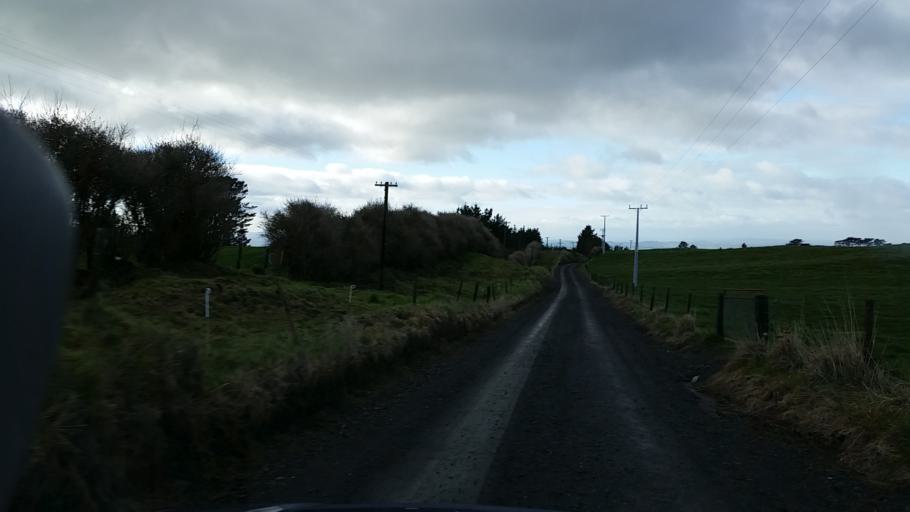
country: NZ
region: Taranaki
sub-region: South Taranaki District
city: Eltham
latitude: -39.3344
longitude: 174.1777
